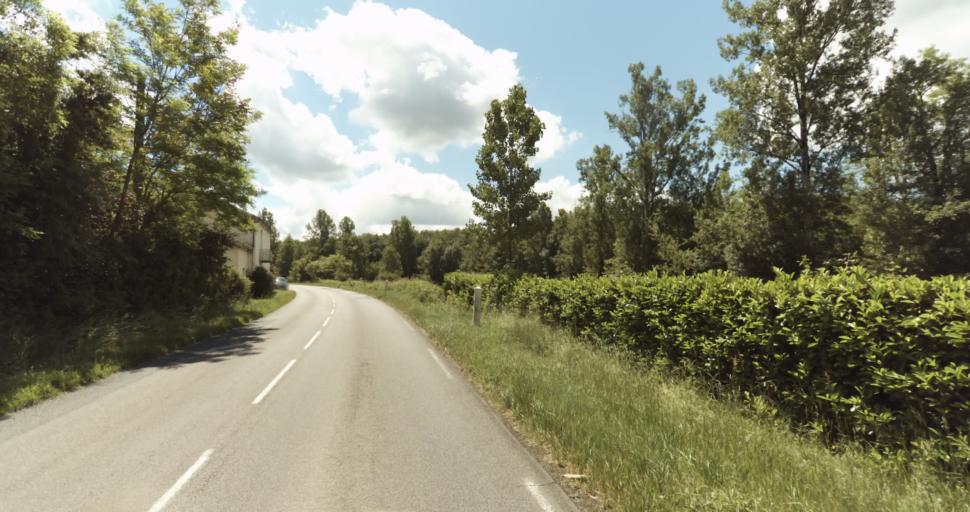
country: FR
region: Aquitaine
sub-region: Departement de la Dordogne
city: Beaumont-du-Perigord
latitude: 44.7889
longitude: 0.7594
